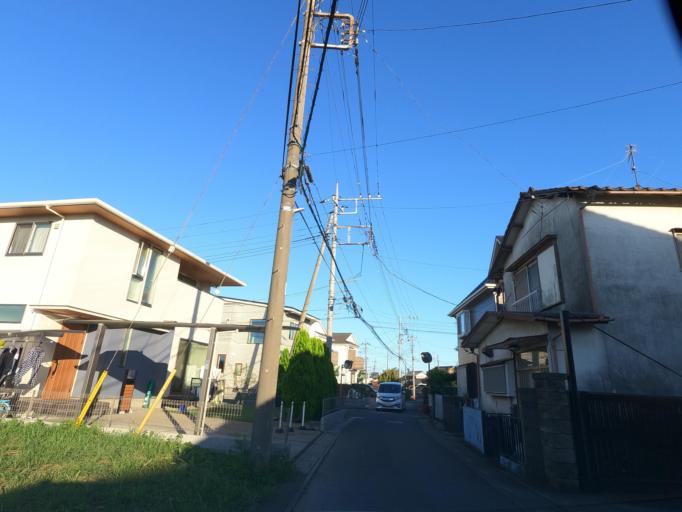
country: JP
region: Saitama
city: Yono
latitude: 35.8937
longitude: 139.5805
